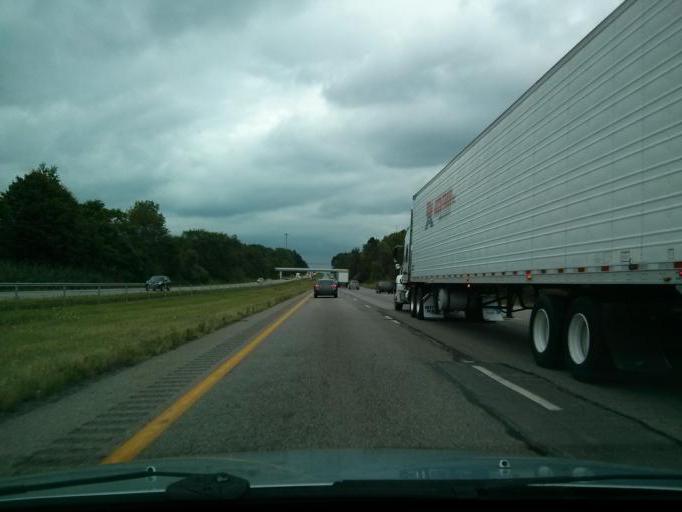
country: US
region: Ohio
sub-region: Portage County
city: Ravenna
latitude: 41.1058
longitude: -81.1506
